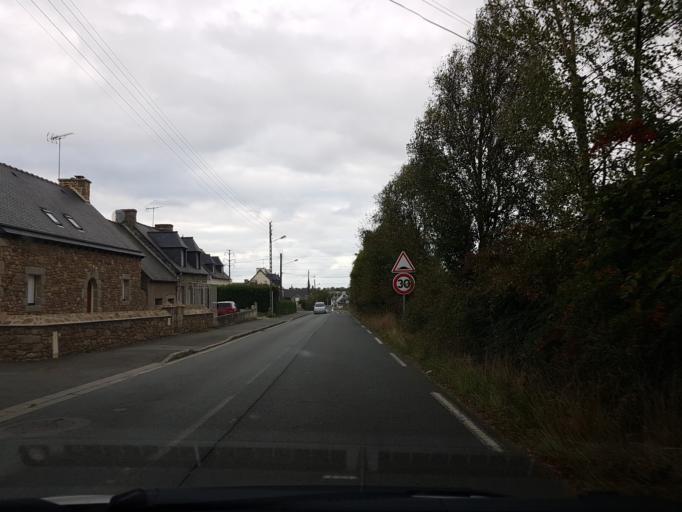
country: FR
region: Brittany
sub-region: Departement des Cotes-d'Armor
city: Langueux
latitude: 48.4681
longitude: -2.7164
